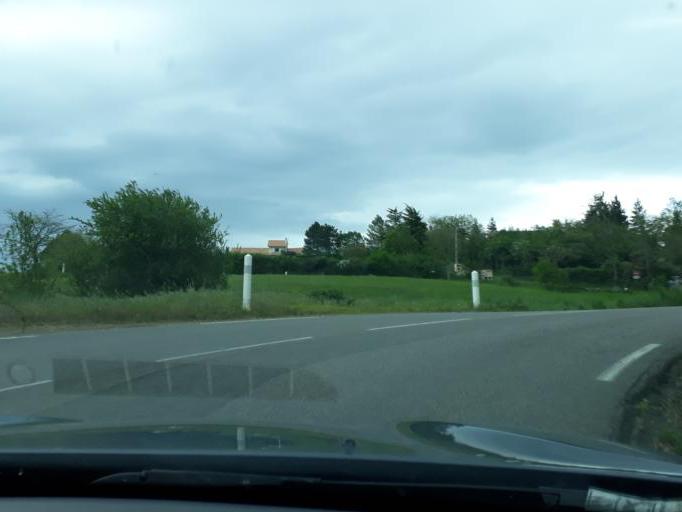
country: FR
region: Rhone-Alpes
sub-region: Departement du Rhone
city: Soucieu-en-Jarrest
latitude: 45.6777
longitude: 4.7098
